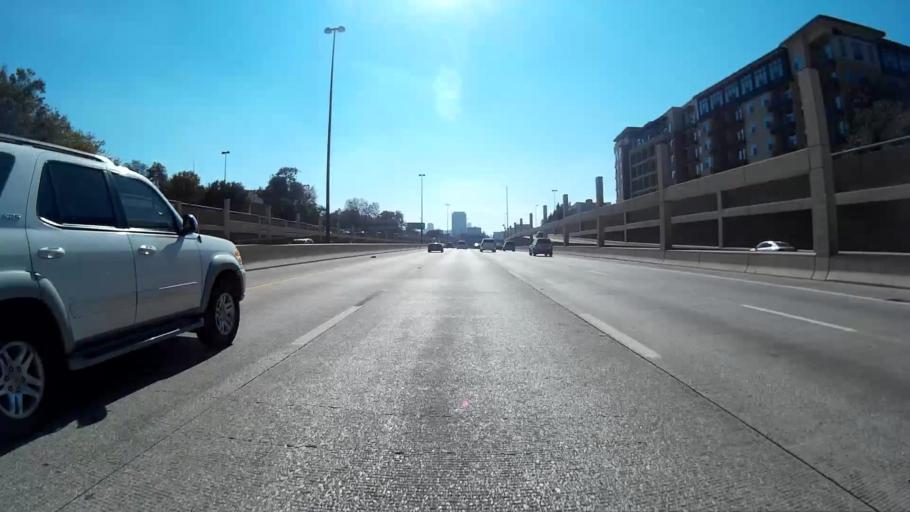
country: US
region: Texas
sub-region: Dallas County
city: Highland Park
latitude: 32.8254
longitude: -96.7845
